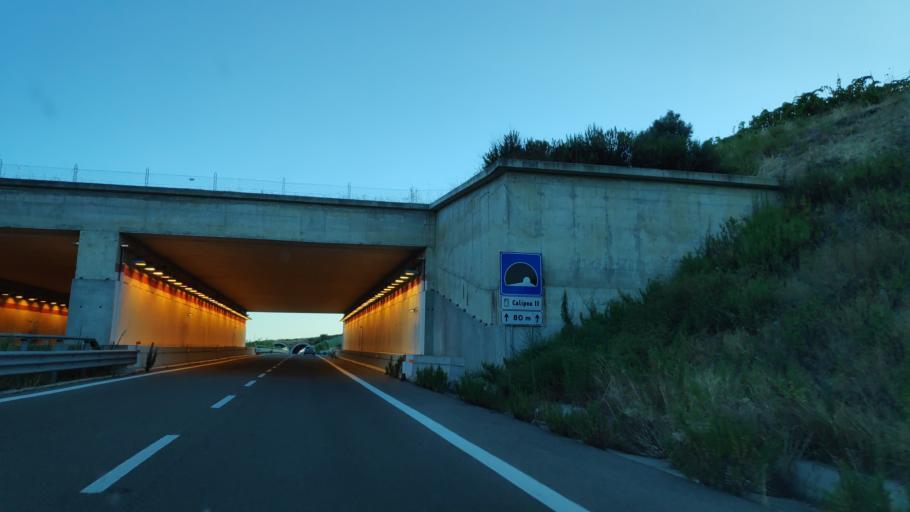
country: IT
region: Calabria
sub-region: Provincia di Reggio Calabria
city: Locri
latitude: 38.2550
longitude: 16.2606
